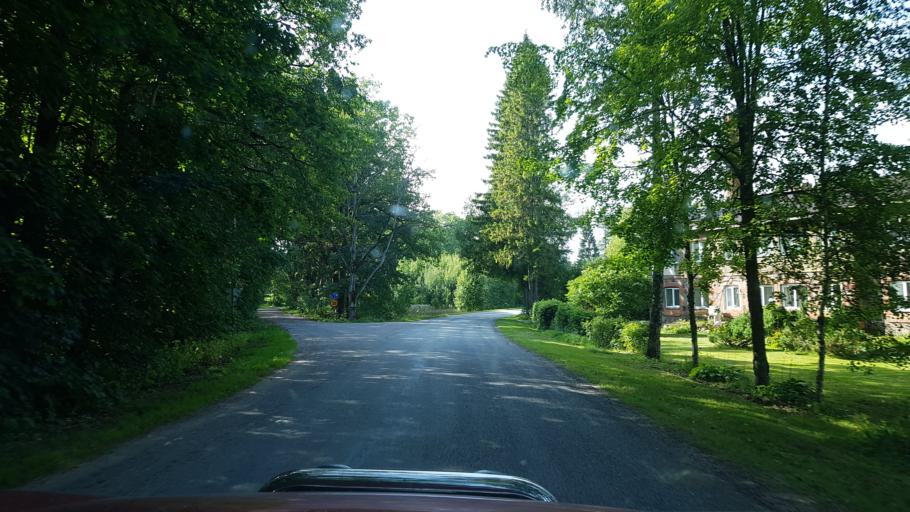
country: EE
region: Viljandimaa
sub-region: Suure-Jaani vald
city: Suure-Jaani
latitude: 58.3605
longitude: 25.3980
